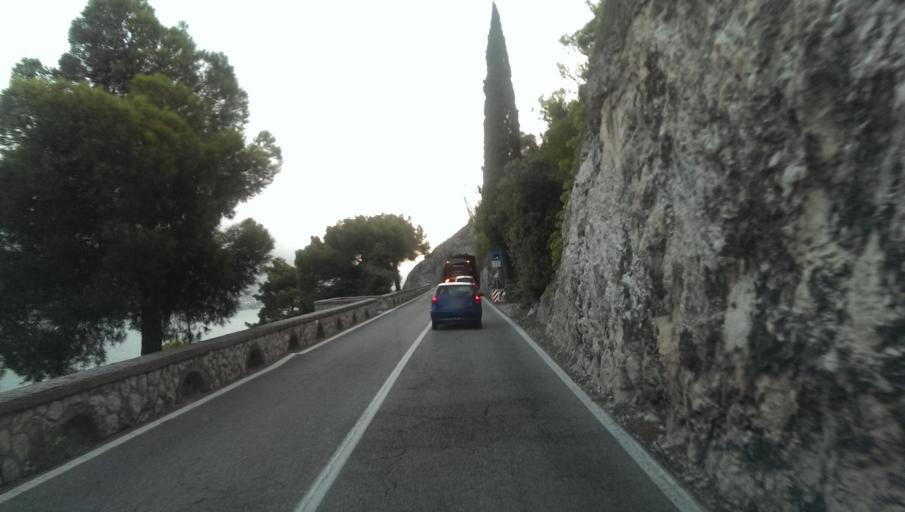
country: IT
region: Lombardy
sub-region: Provincia di Brescia
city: Limone sul Garda
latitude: 45.8303
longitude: 10.8228
